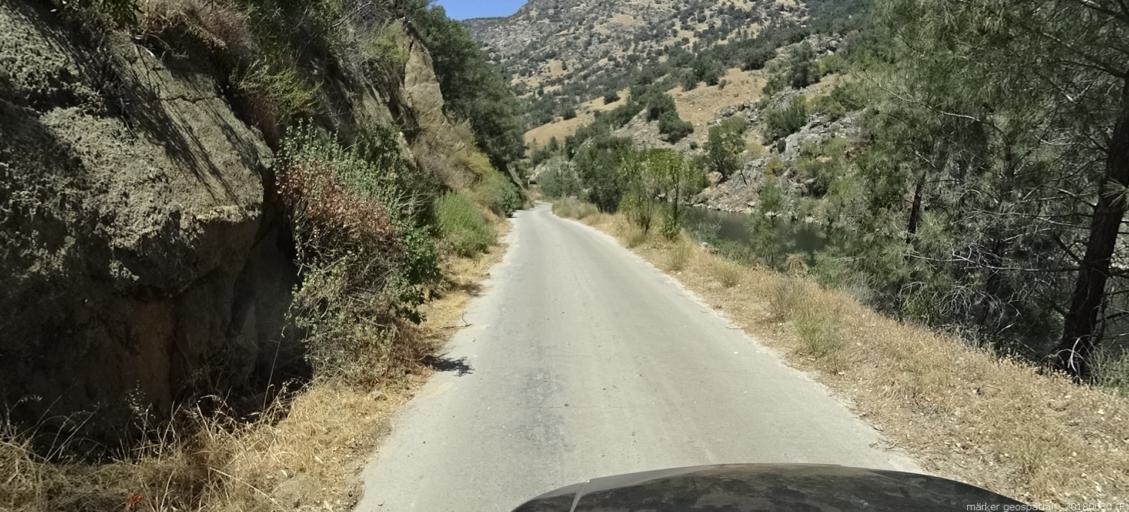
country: US
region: California
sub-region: Fresno County
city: Auberry
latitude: 37.1561
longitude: -119.4045
